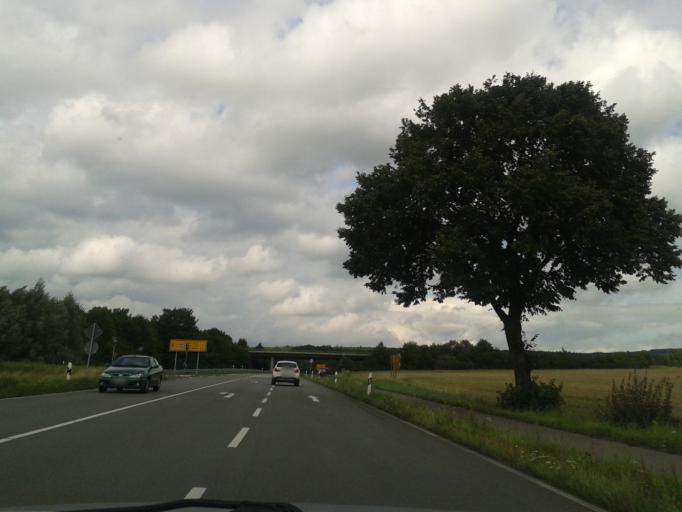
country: DE
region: North Rhine-Westphalia
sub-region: Regierungsbezirk Detmold
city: Schlangen
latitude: 51.8194
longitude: 8.8514
